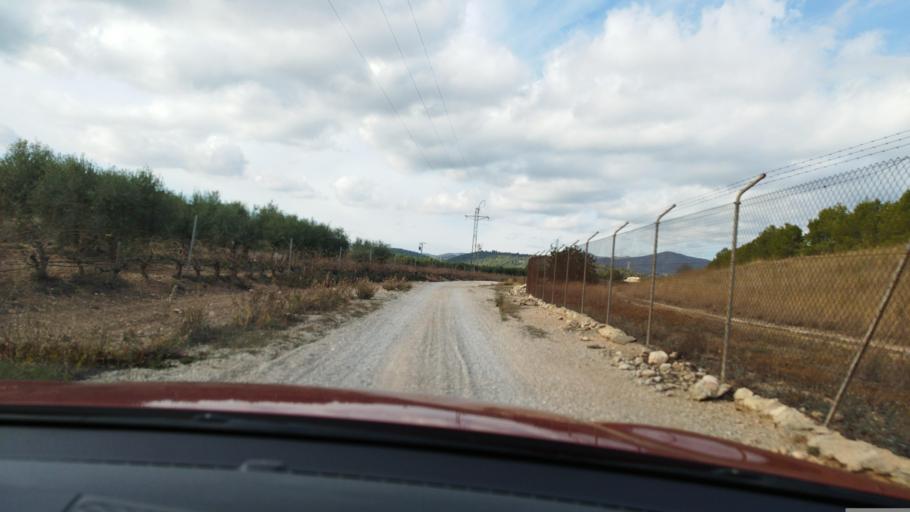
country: ES
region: Catalonia
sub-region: Provincia de Tarragona
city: Albinyana
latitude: 41.2601
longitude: 1.5026
